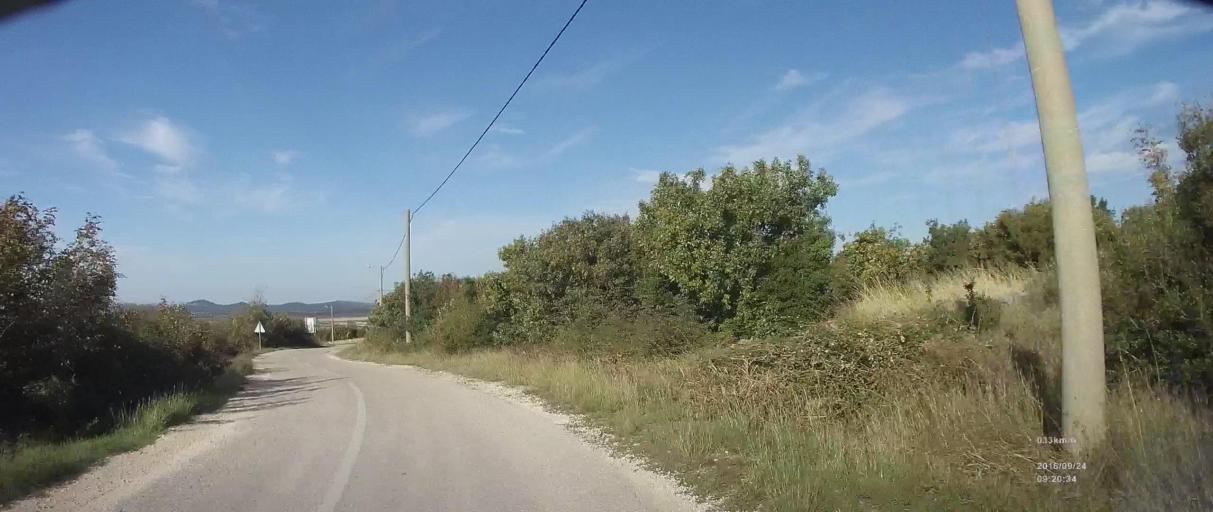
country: HR
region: Zadarska
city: Polaca
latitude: 44.0689
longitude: 15.4963
